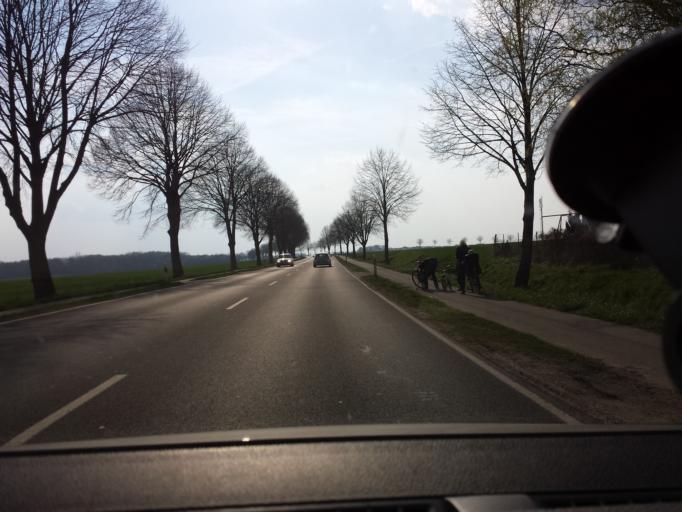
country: DE
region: Lower Saxony
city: Braunschweig
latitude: 52.2693
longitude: 10.4782
